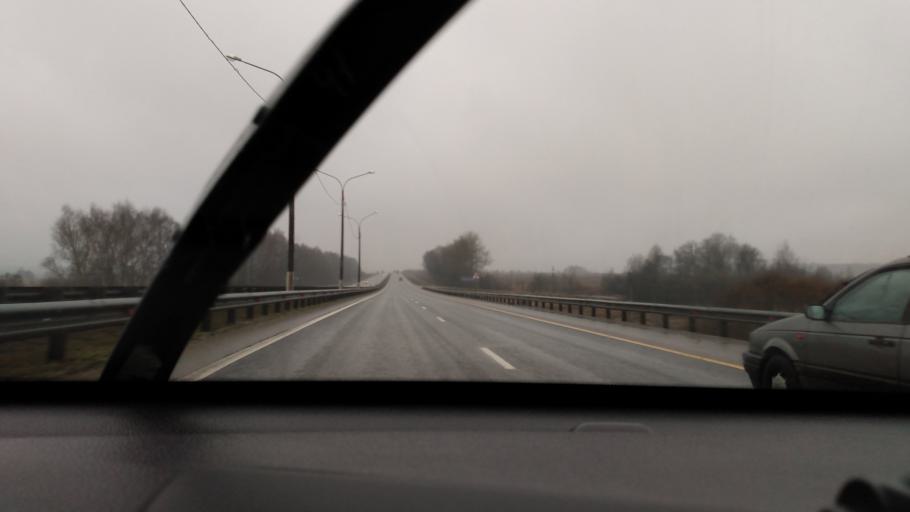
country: RU
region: Tula
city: Gritsovskiy
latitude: 54.2429
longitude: 38.1359
